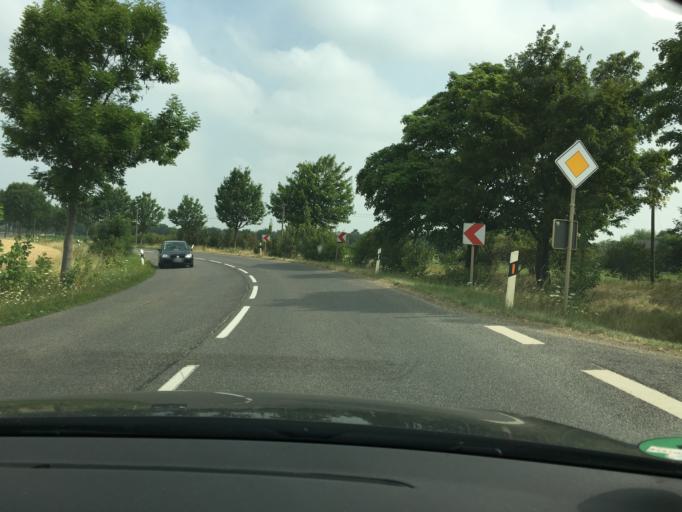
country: DE
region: North Rhine-Westphalia
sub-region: Regierungsbezirk Koln
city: Norvenich
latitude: 50.7994
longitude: 6.5863
